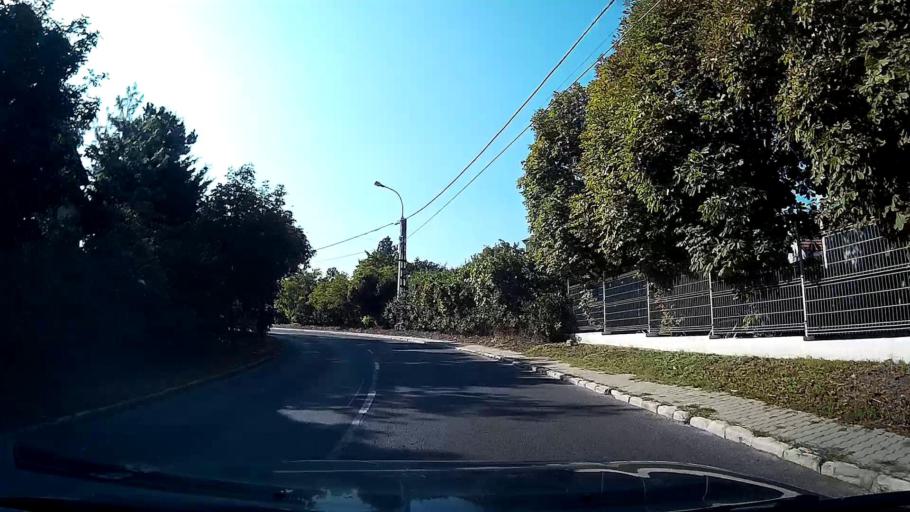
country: HU
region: Budapest
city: Budapest XXII. keruelet
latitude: 47.4160
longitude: 19.0140
